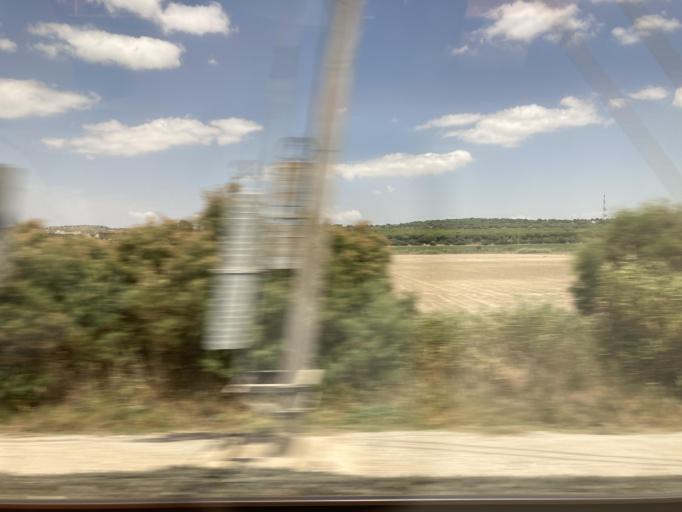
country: ES
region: Andalusia
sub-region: Provincia de Cadiz
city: El Puerto de Santa Maria
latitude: 36.6181
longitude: -6.1794
